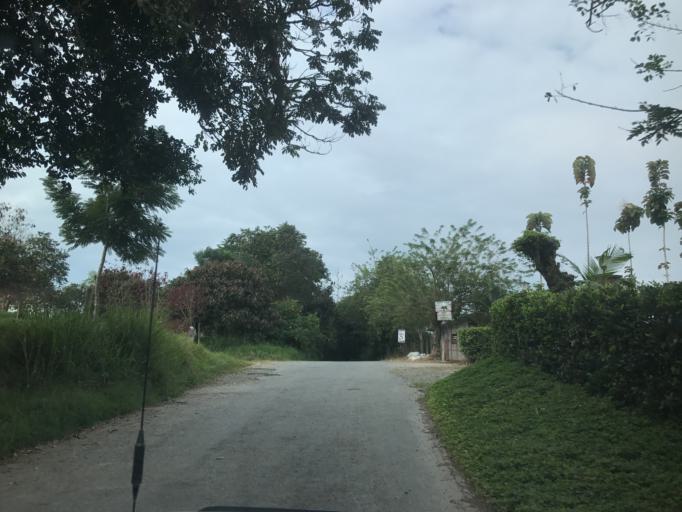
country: CO
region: Quindio
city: Montenegro
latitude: 4.5410
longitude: -75.8319
